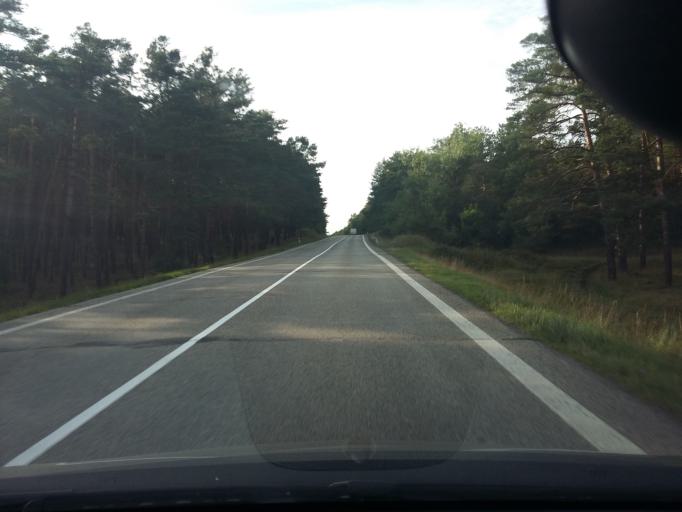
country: SK
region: Bratislavsky
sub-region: Okres Malacky
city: Malacky
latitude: 48.3925
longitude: 17.0954
